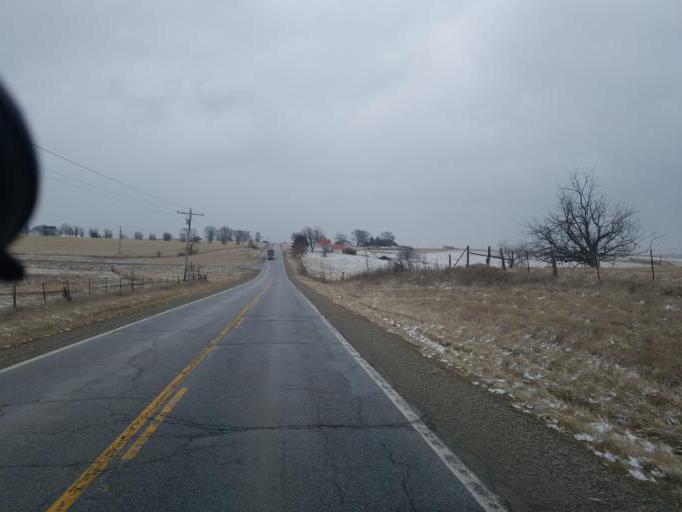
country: US
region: Missouri
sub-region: Putnam County
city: Unionville
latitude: 40.4723
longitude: -92.9587
